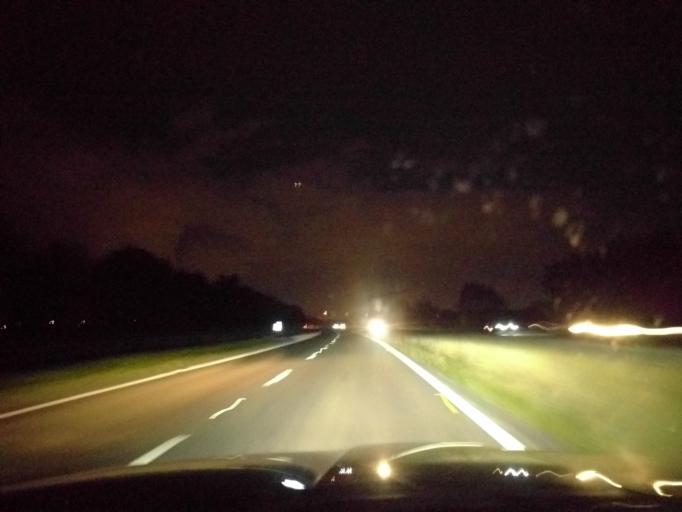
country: GB
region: England
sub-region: Northumberland
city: Seghill
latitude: 55.0440
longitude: -1.5500
